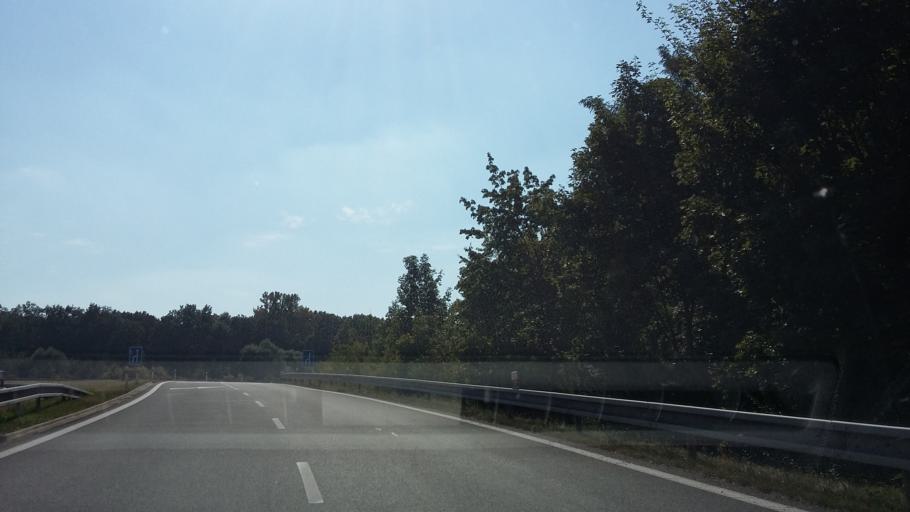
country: CZ
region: Central Bohemia
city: Libice nad Cidlinou
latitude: 50.1197
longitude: 15.1645
